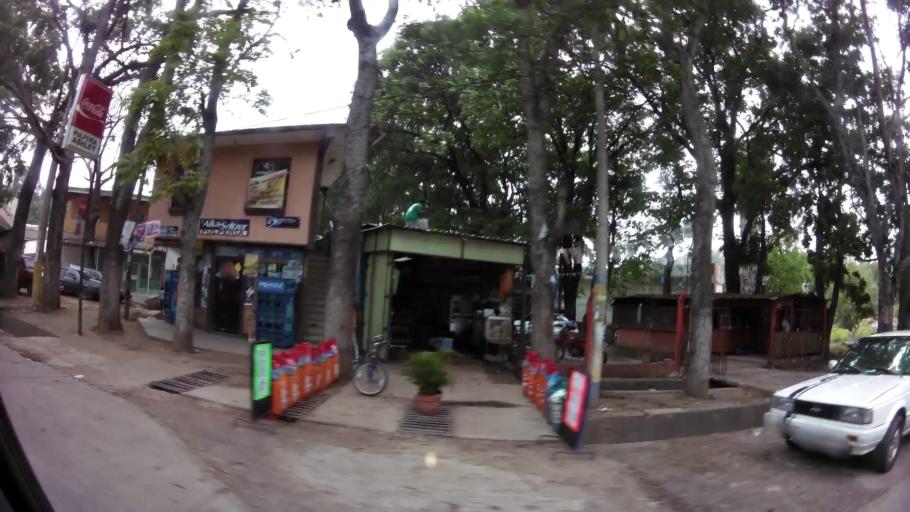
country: HN
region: Francisco Morazan
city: Tegucigalpa
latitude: 14.0637
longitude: -87.2010
